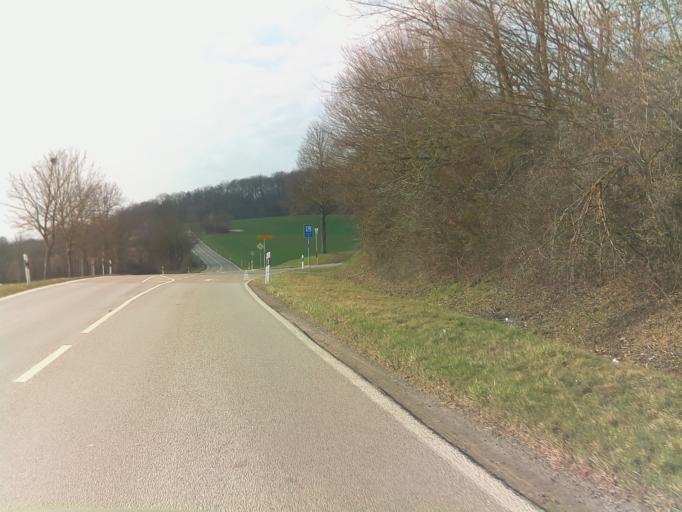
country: DE
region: Baden-Wuerttemberg
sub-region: Regierungsbezirk Stuttgart
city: Gemmingen
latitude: 49.1677
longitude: 8.9692
